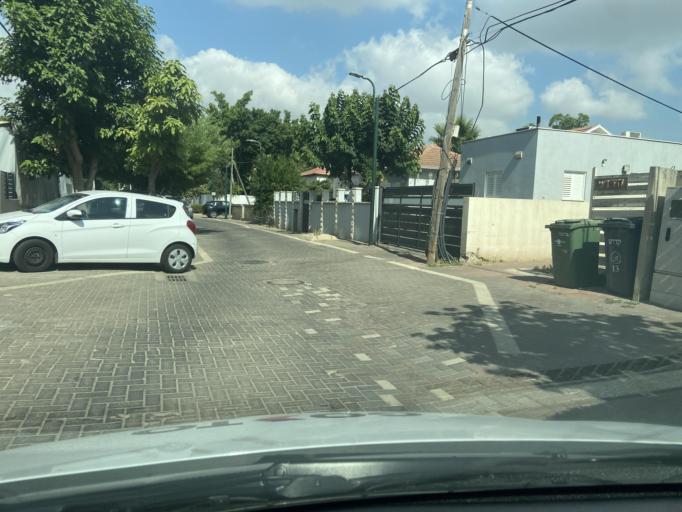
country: IL
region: Central District
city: Yehud
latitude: 32.0315
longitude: 34.8847
